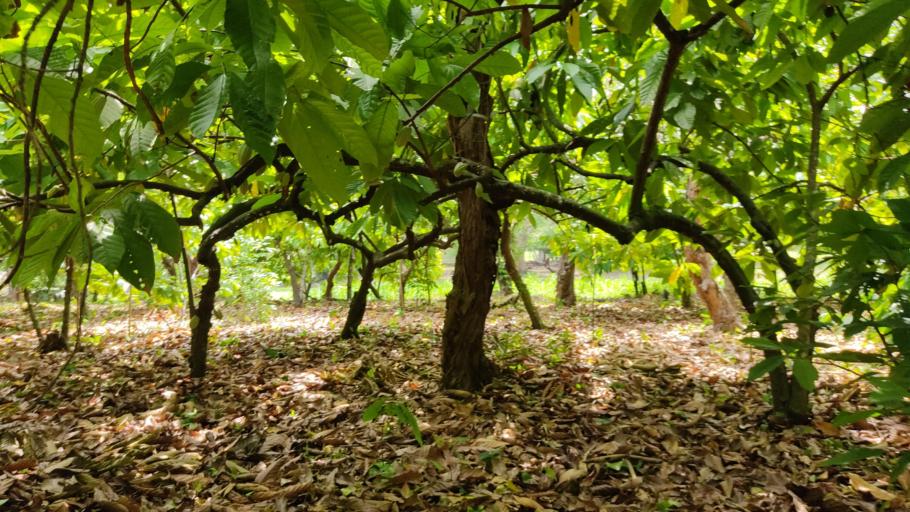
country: MX
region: Tabasco
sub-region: Comalcalco
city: Ignacio Zaragoza 1ra. Seccion
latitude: 18.3184
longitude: -93.3257
